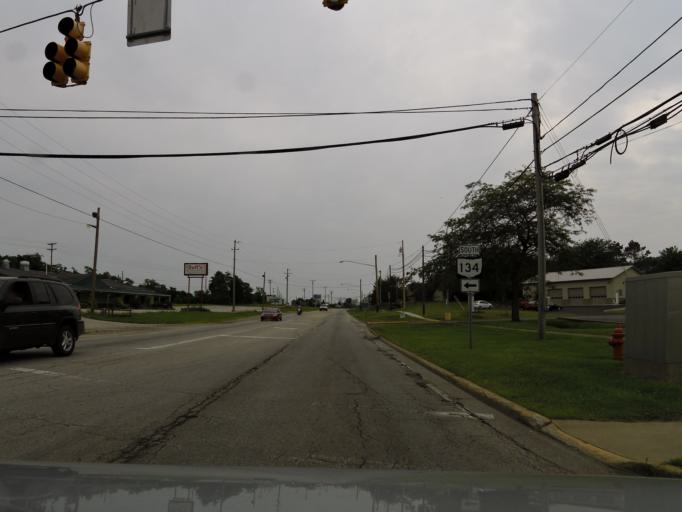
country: US
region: Ohio
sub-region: Clinton County
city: Wilmington
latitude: 39.4321
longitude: -83.8312
